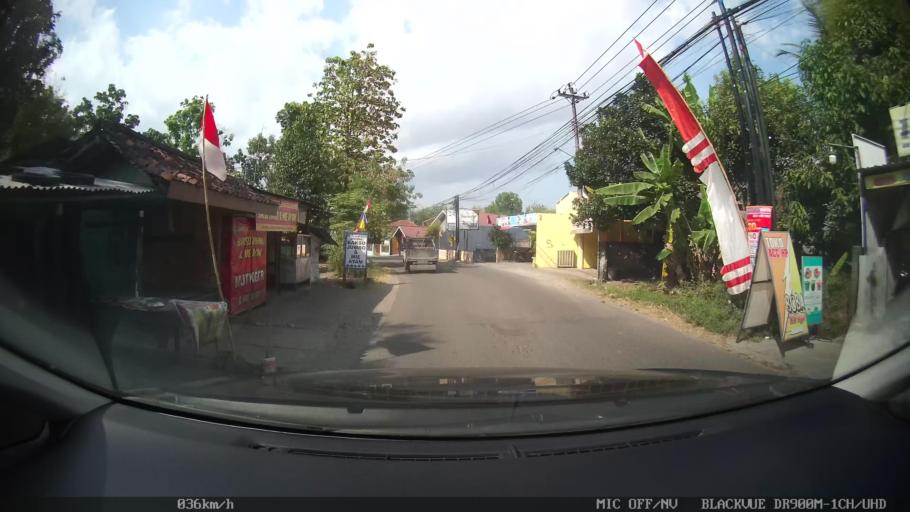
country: ID
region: Daerah Istimewa Yogyakarta
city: Kasihan
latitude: -7.8392
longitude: 110.3149
